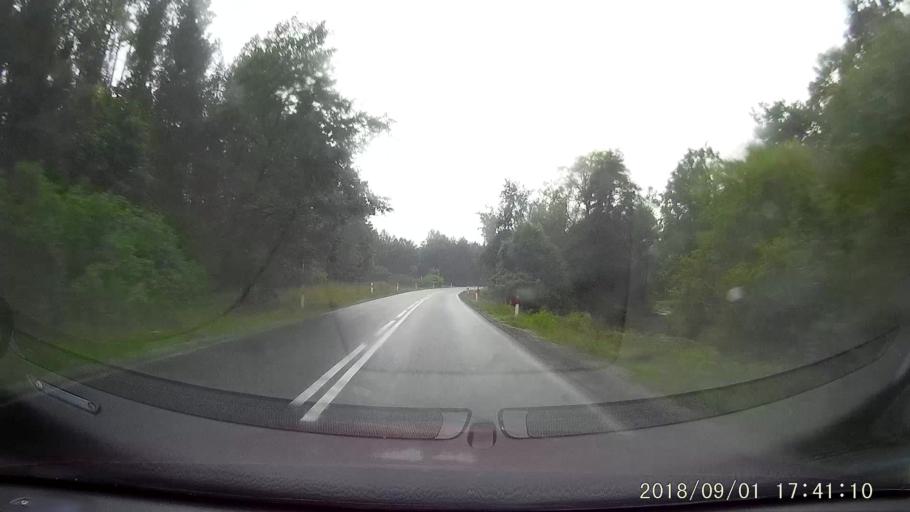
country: PL
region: Lubusz
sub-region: Powiat zaganski
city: Zagan
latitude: 51.5694
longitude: 15.2695
